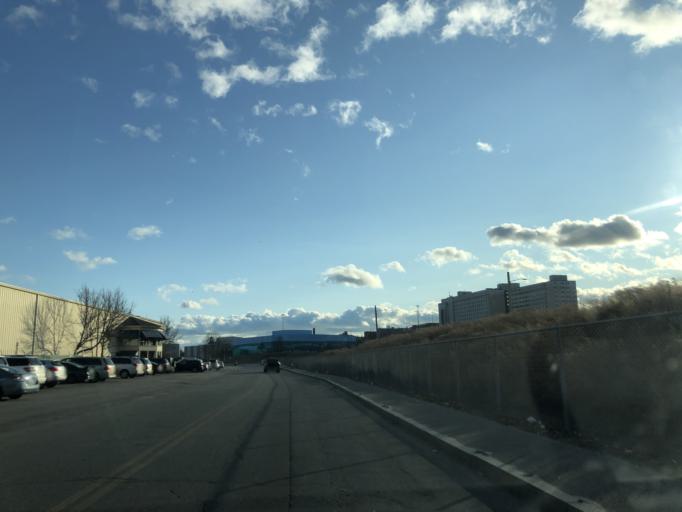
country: US
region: Massachusetts
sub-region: Bristol County
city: New Bedford
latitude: 41.6429
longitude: -70.9242
